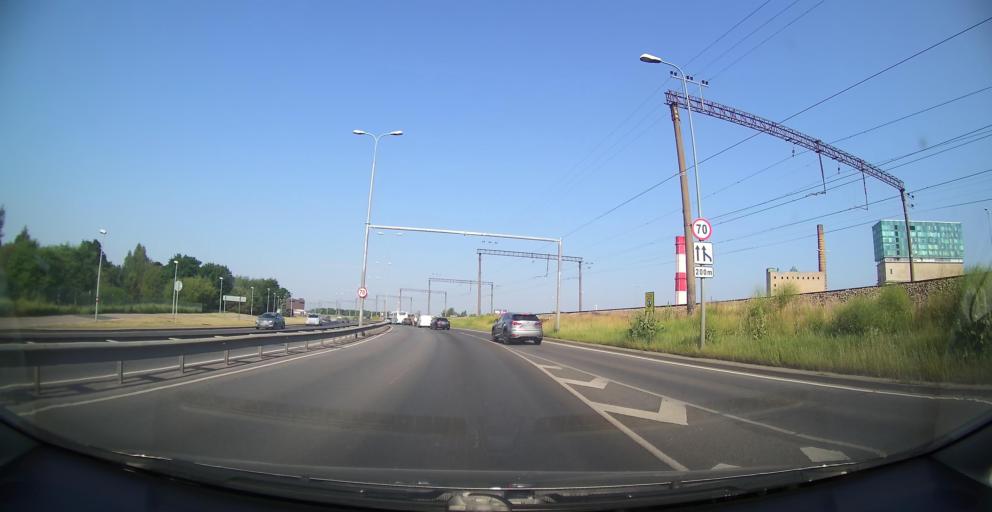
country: EE
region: Harju
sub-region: Tallinna linn
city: Tallinn
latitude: 59.4208
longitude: 24.7744
